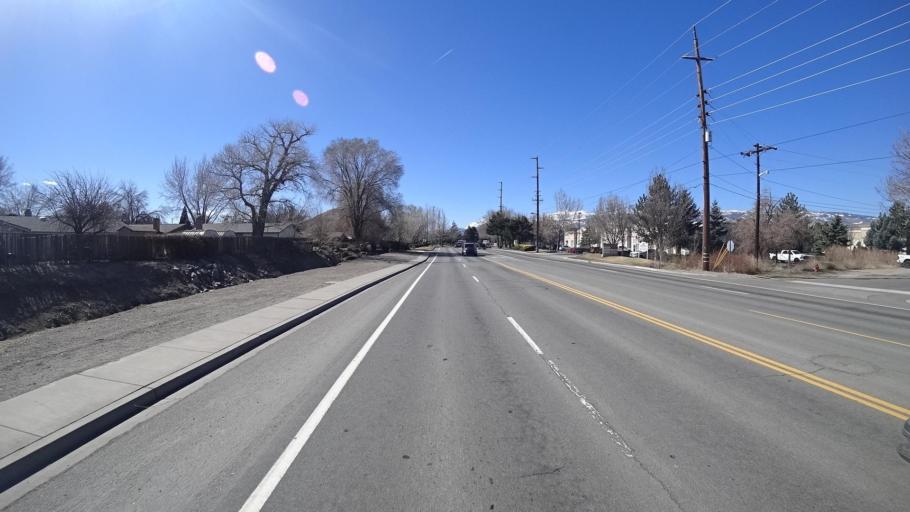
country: US
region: Nevada
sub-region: Washoe County
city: Sparks
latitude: 39.4912
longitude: -119.7564
